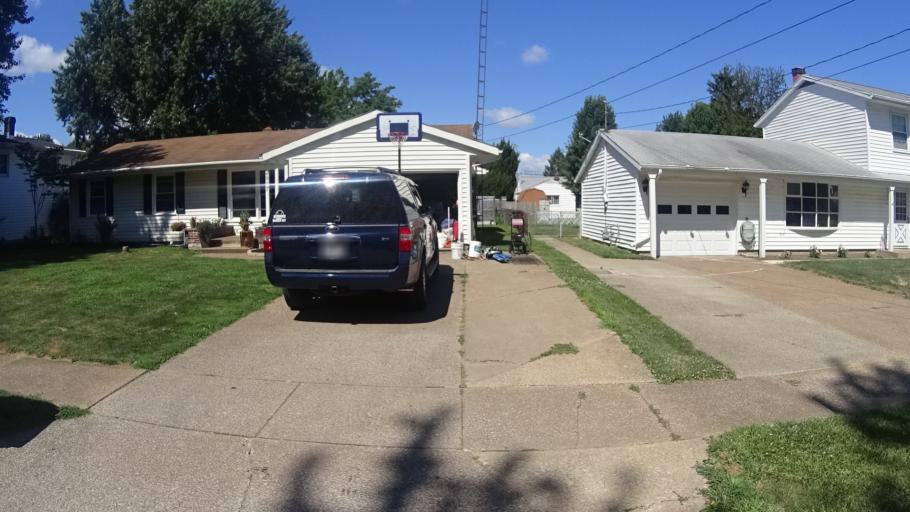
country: US
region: Ohio
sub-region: Erie County
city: Sandusky
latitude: 41.4271
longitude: -82.6554
